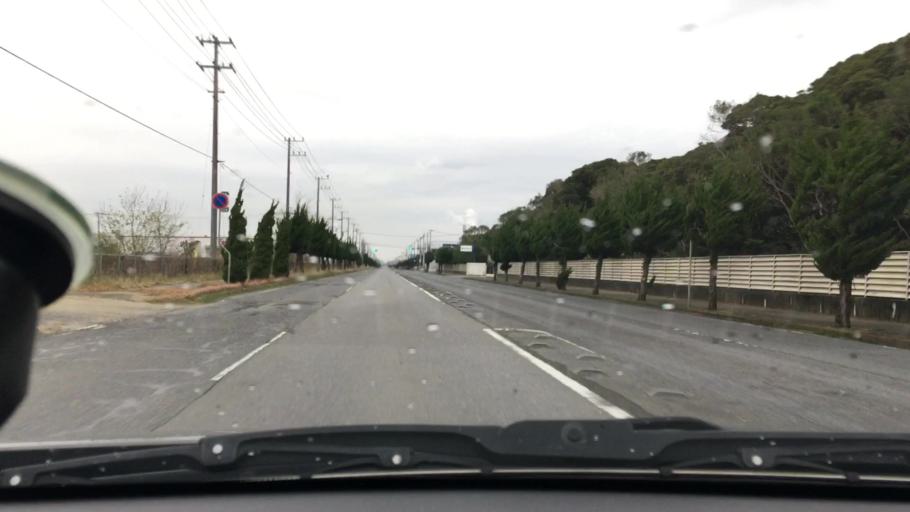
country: JP
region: Chiba
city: Omigawa
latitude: 35.8537
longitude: 140.7190
